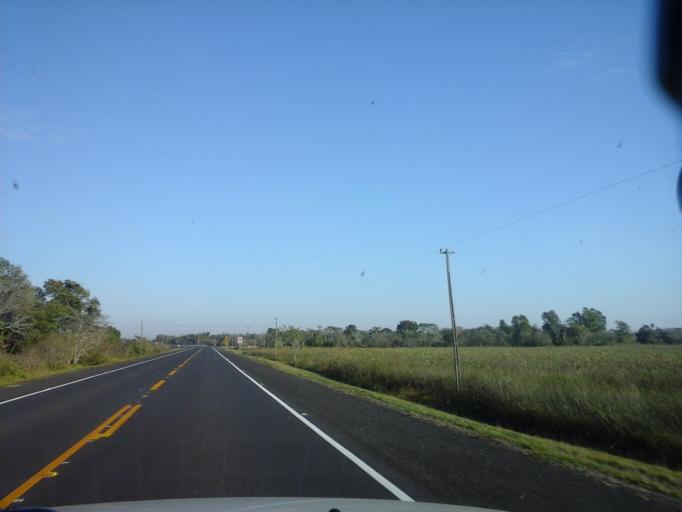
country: PY
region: Neembucu
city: Pilar
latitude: -26.8755
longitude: -57.8984
